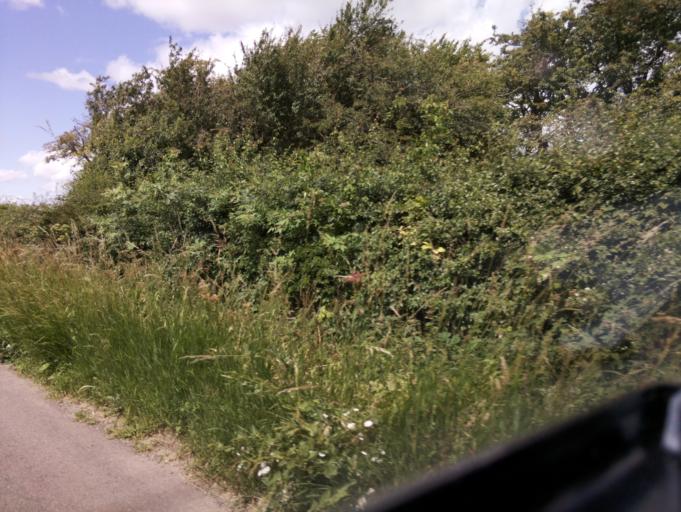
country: GB
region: England
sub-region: Nottinghamshire
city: Burton Joyce
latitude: 53.0049
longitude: -1.0786
